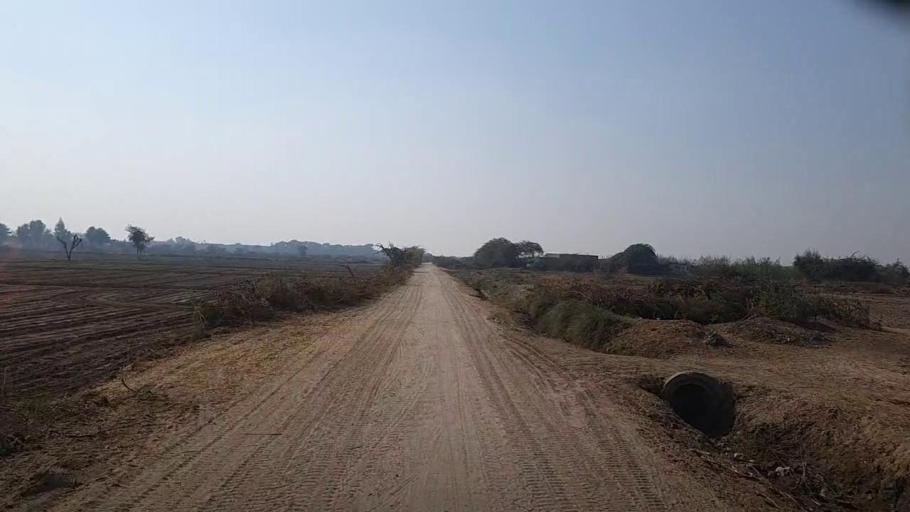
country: PK
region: Sindh
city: Bozdar
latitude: 27.2411
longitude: 68.6018
